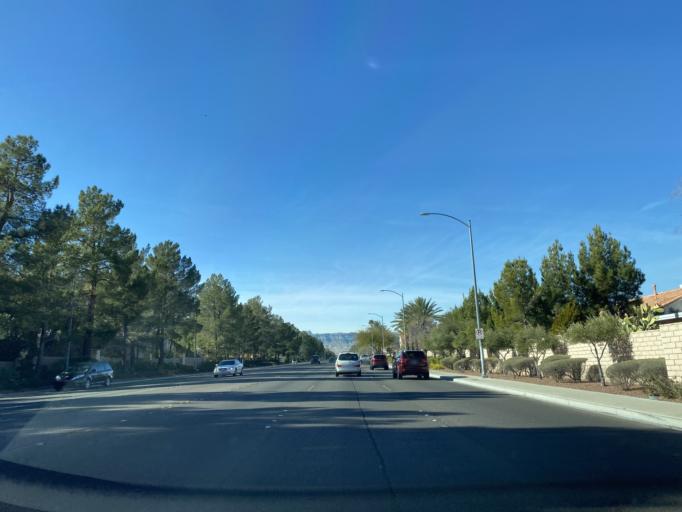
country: US
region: Nevada
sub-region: Clark County
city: Spring Valley
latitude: 36.0998
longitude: -115.2656
